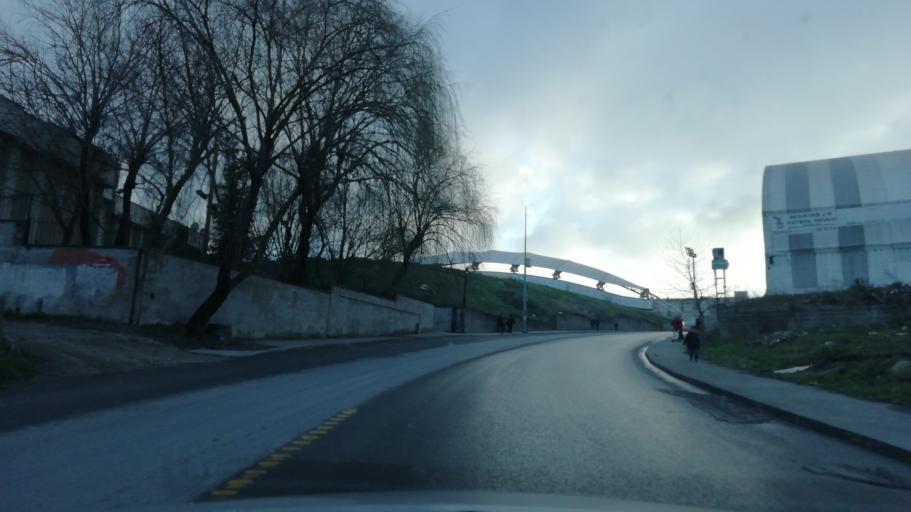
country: TR
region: Istanbul
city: Esenyurt
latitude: 41.0158
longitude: 28.7004
